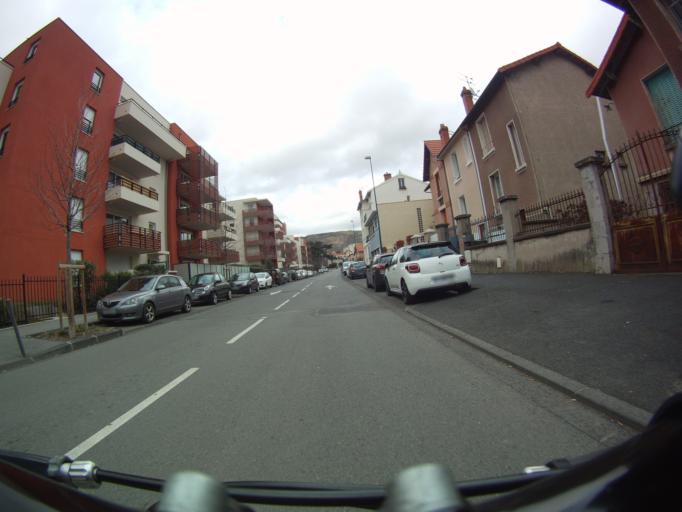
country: FR
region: Auvergne
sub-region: Departement du Puy-de-Dome
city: Clermont-Ferrand
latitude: 45.7873
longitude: 3.0898
